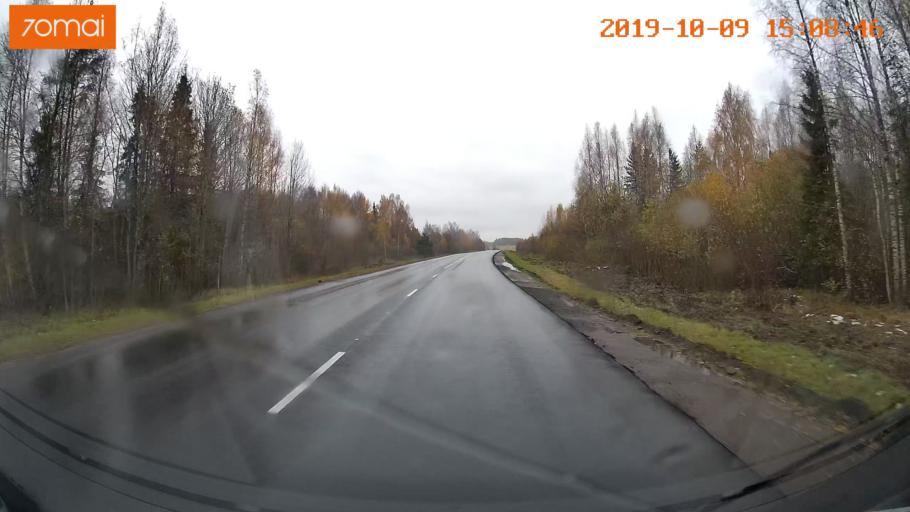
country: RU
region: Kostroma
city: Susanino
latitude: 58.2014
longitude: 41.6518
